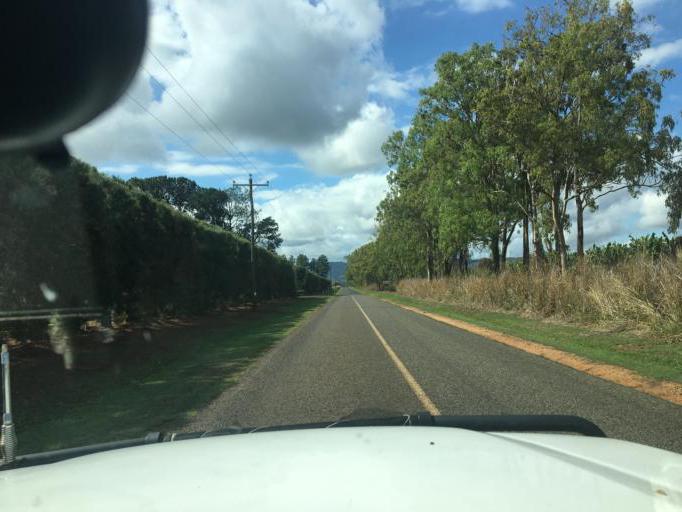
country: AU
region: Queensland
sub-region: Tablelands
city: Mareeba
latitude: -17.1093
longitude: 145.4108
